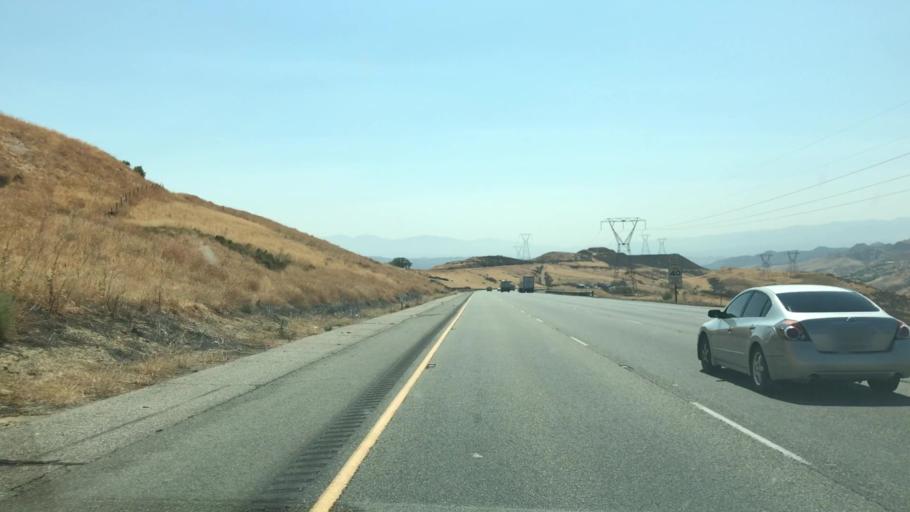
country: US
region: California
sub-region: Los Angeles County
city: Castaic
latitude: 34.5391
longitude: -118.6487
